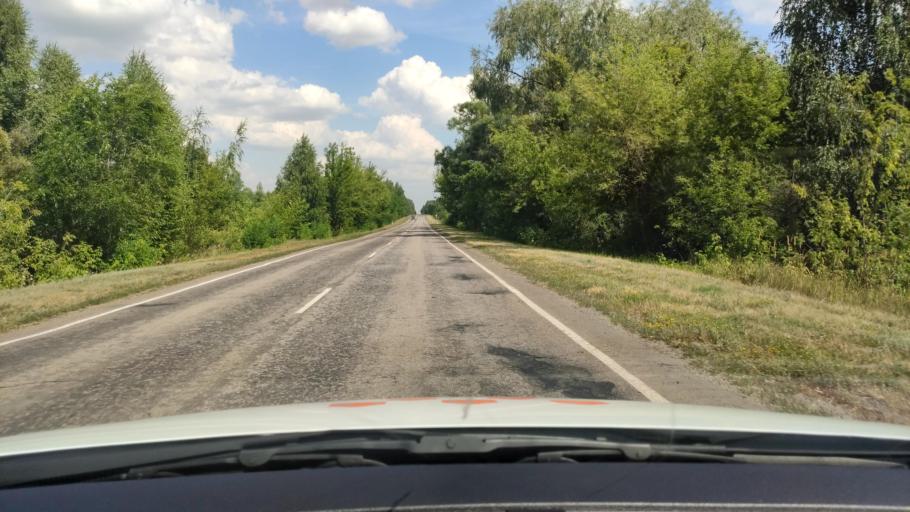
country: RU
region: Voronezj
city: Ertil'
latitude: 51.7834
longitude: 40.5637
